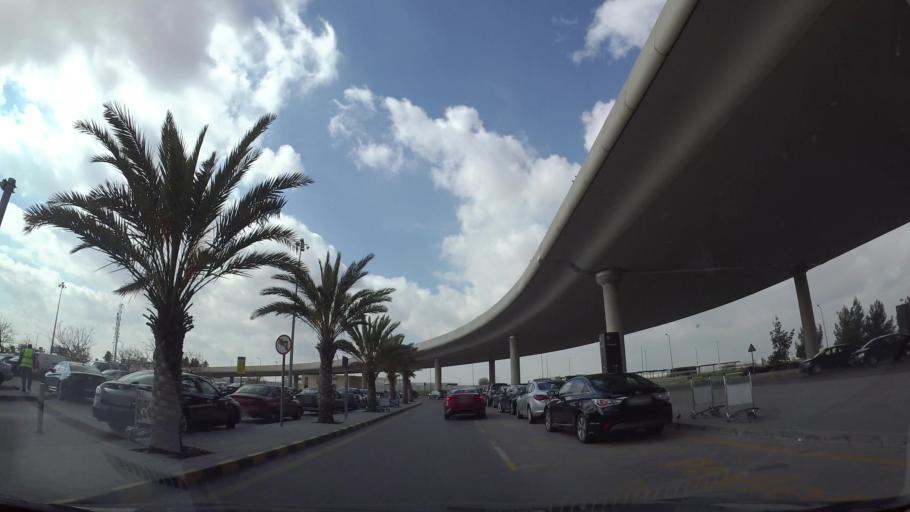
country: JO
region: Amman
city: Al Jizah
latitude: 31.7228
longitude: 35.9849
